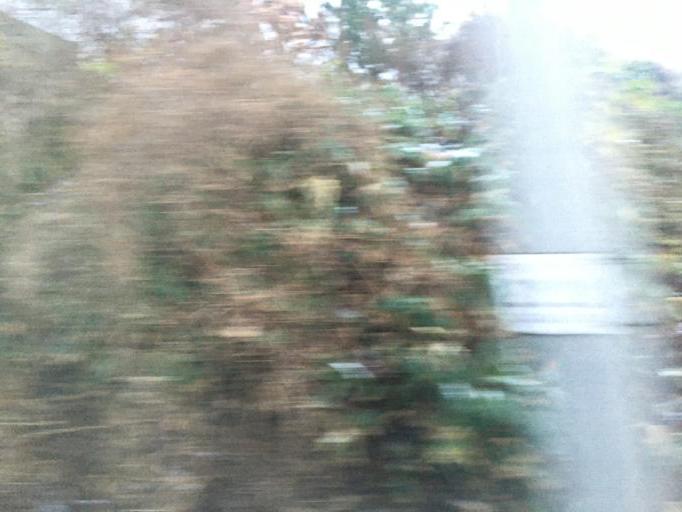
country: JP
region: Aomori
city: Aomori Shi
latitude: 40.8286
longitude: 140.6753
